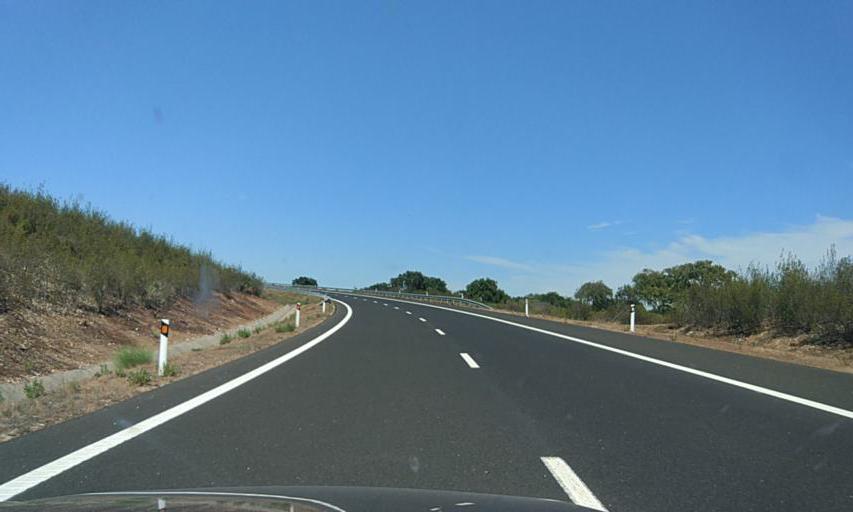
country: PT
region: Santarem
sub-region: Benavente
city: Poceirao
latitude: 38.8999
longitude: -8.7840
